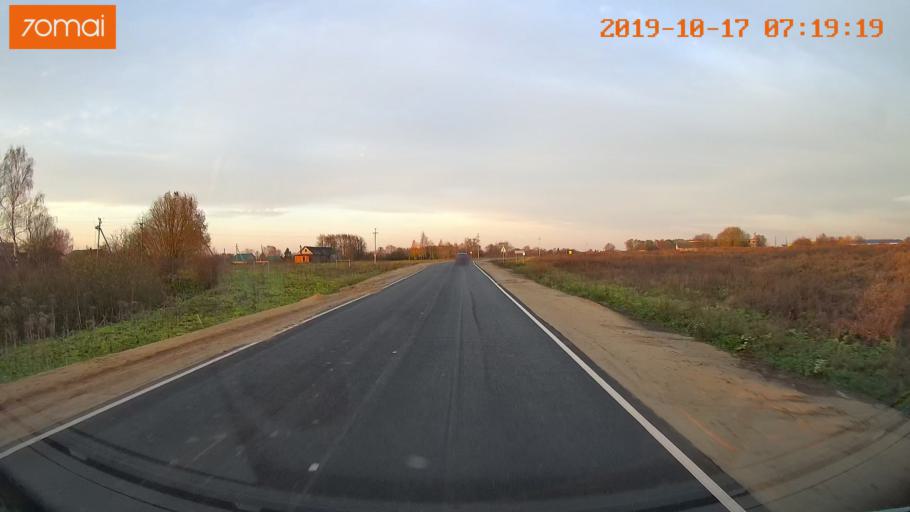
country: RU
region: Ivanovo
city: Gavrilov Posad
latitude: 56.3459
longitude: 40.2016
